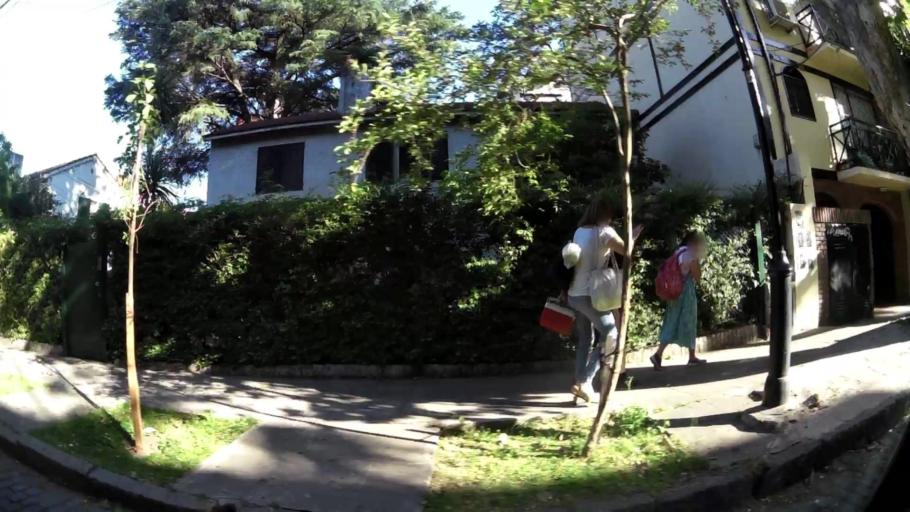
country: AR
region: Buenos Aires
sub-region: Partido de San Isidro
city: San Isidro
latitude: -34.4720
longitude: -58.5105
